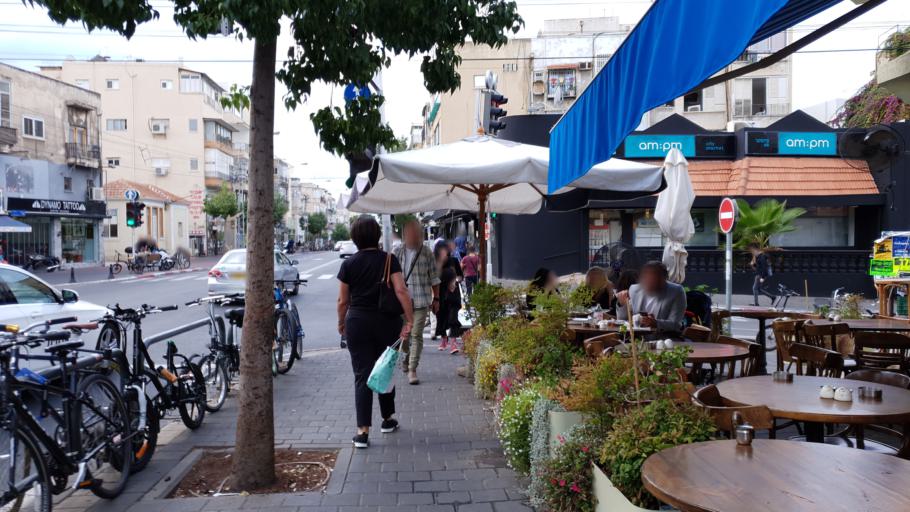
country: IL
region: Tel Aviv
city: Tel Aviv
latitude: 32.0758
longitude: 34.7720
